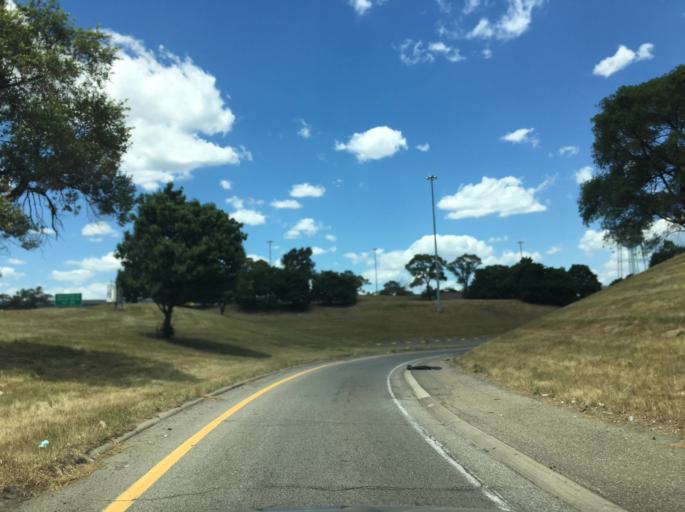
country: US
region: Michigan
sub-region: Wayne County
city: Highland Park
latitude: 42.4071
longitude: -83.0766
